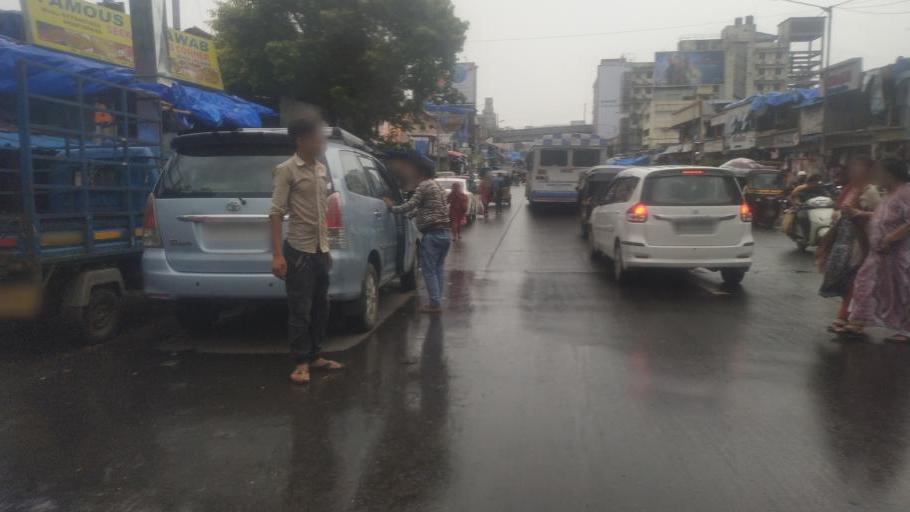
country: IN
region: Maharashtra
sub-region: Mumbai Suburban
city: Powai
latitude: 19.1240
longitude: 72.8467
